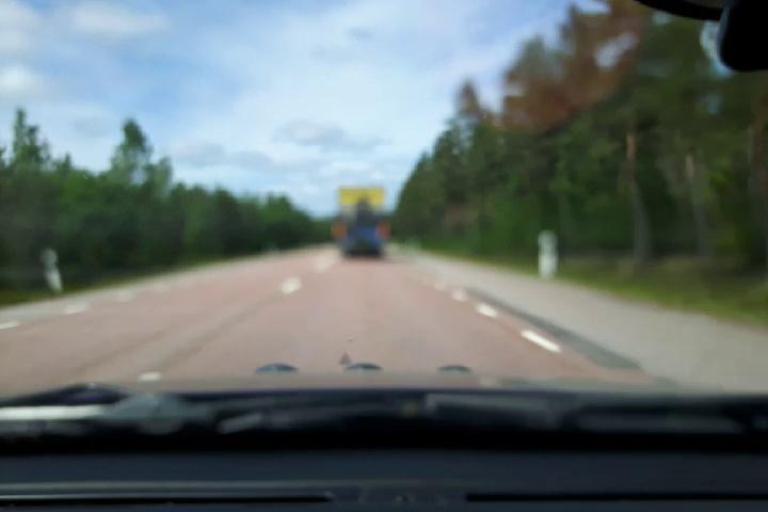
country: SE
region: Uppsala
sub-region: Osthammars Kommun
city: Bjorklinge
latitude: 60.1784
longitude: 17.4819
